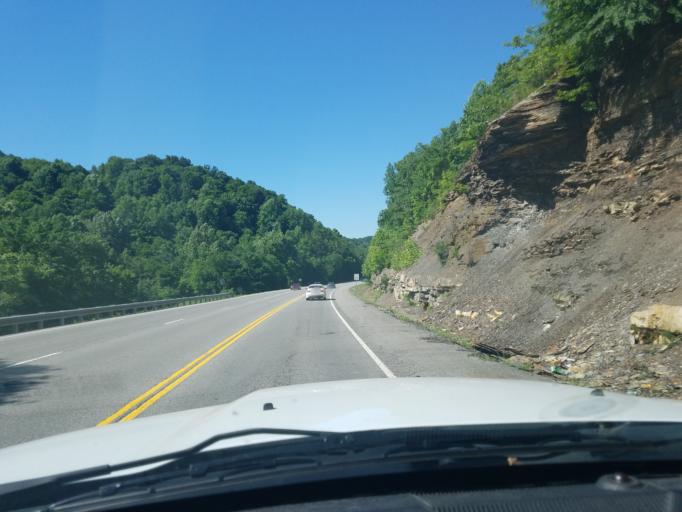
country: US
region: Tennessee
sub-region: Sumner County
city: Westmoreland
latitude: 36.5365
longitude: -86.2447
